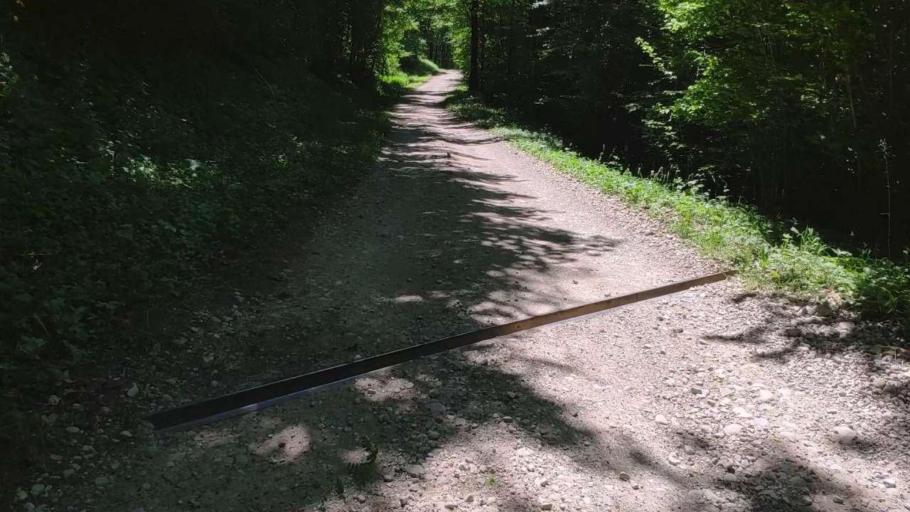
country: FR
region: Franche-Comte
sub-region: Departement du Jura
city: Perrigny
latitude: 46.7347
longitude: 5.6559
